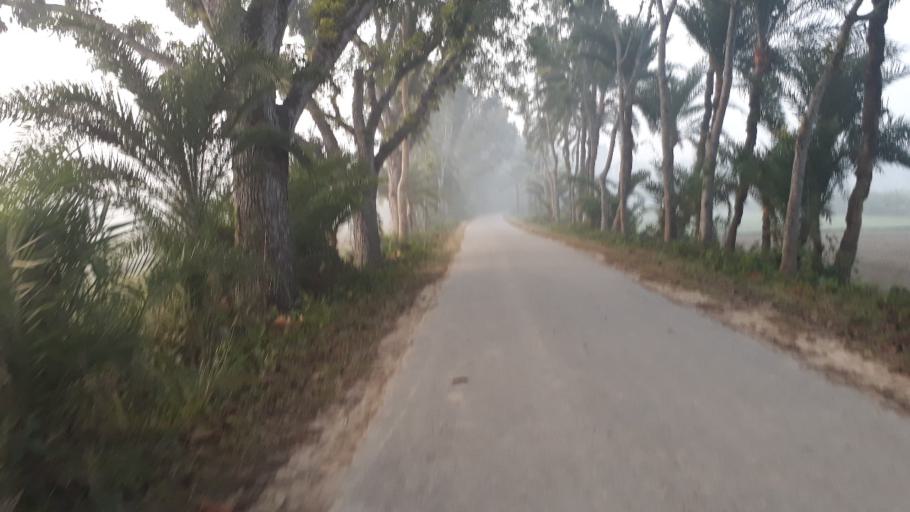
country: BD
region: Khulna
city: Jhingergacha
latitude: 23.2609
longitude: 88.9321
